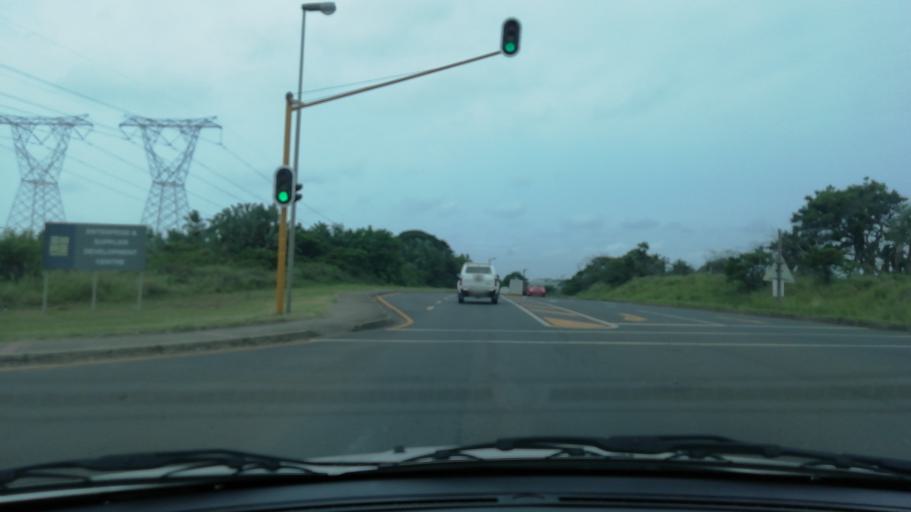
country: ZA
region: KwaZulu-Natal
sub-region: uThungulu District Municipality
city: Richards Bay
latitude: -28.7646
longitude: 32.0376
